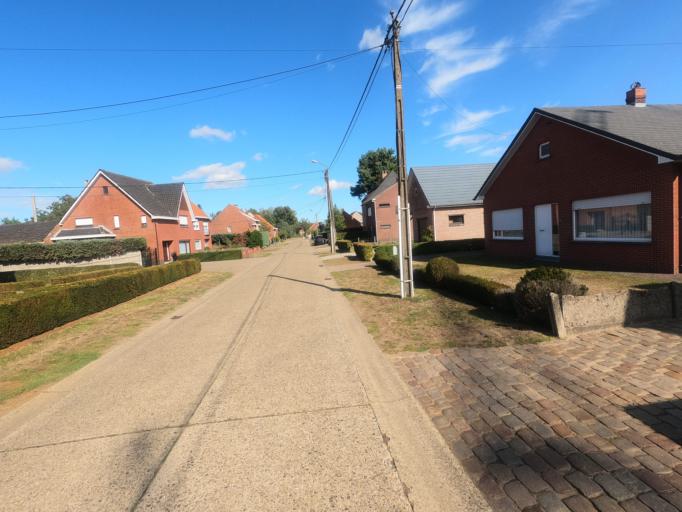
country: BE
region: Flanders
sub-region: Provincie Antwerpen
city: Lille
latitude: 51.2335
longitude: 4.8343
